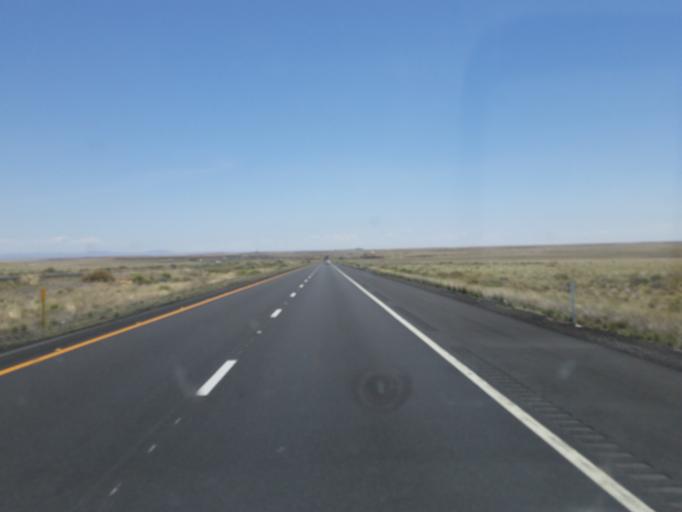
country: US
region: Arizona
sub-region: Coconino County
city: LeChee
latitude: 35.1172
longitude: -111.1208
